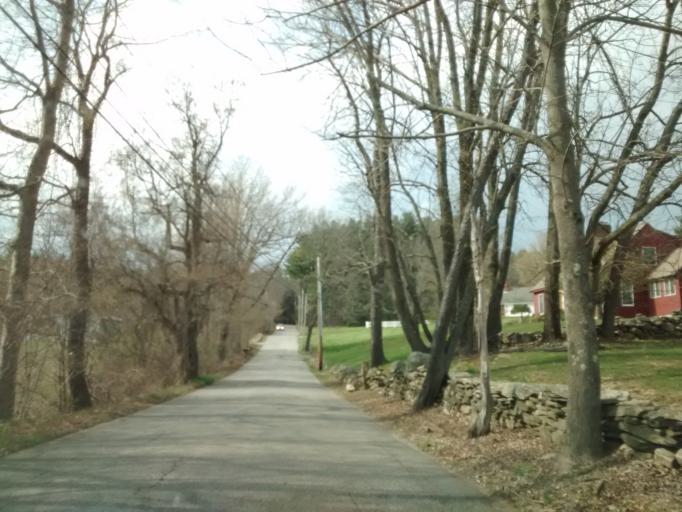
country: US
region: Massachusetts
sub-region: Worcester County
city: Sutton
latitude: 42.1492
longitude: -71.7979
